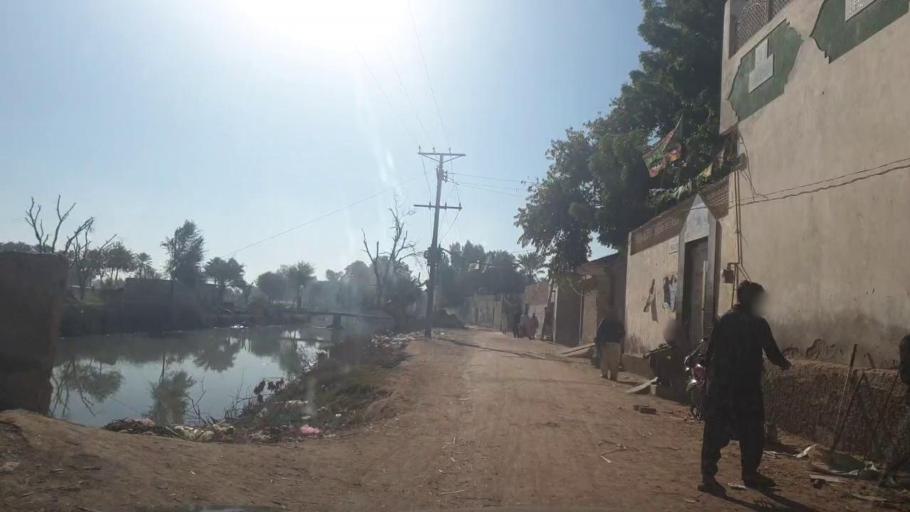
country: PK
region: Sindh
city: Ghotki
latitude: 27.9797
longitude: 69.3268
